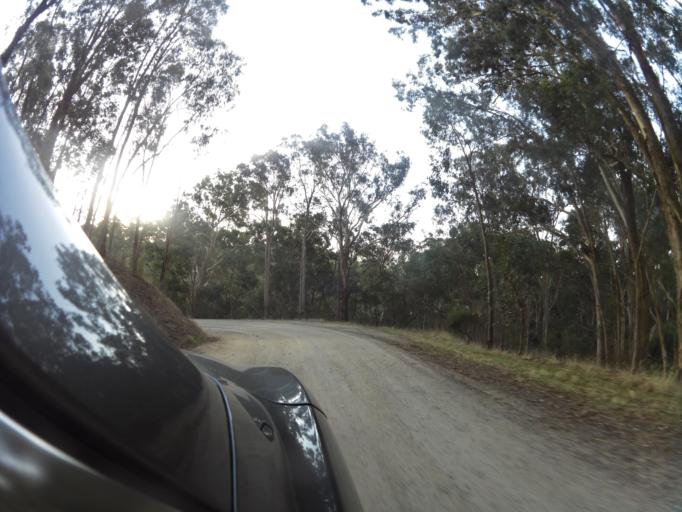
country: AU
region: Victoria
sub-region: Murrindindi
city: Alexandra
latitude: -37.1332
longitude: 145.5231
